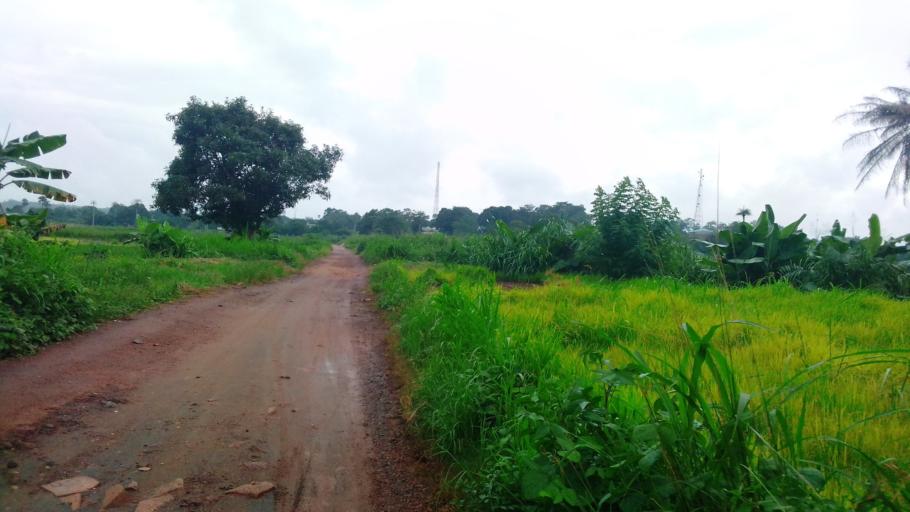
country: SL
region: Northern Province
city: Lunsar
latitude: 8.6882
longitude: -12.5229
